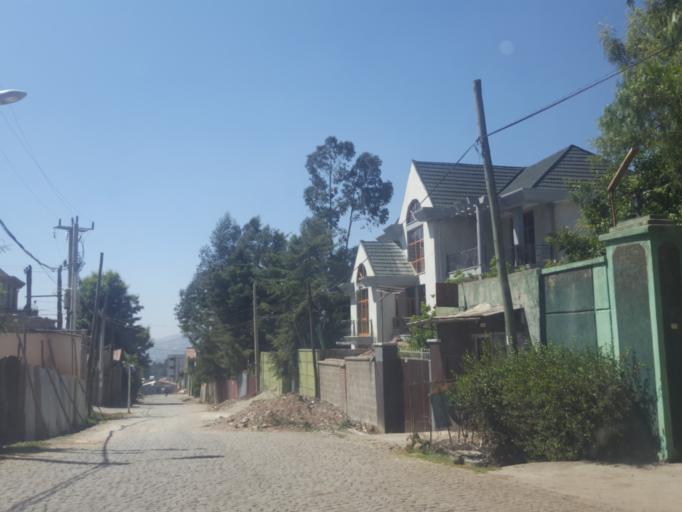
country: ET
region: Adis Abeba
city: Addis Ababa
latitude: 9.0583
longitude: 38.7237
